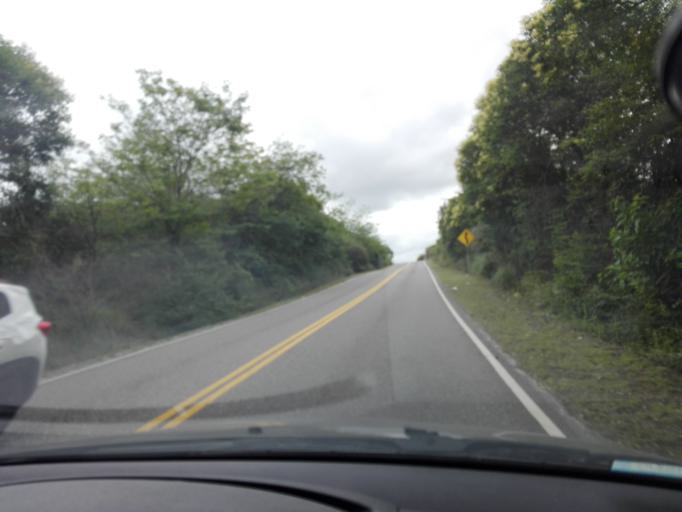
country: AR
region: Cordoba
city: Cuesta Blanca
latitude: -31.5913
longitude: -64.5757
